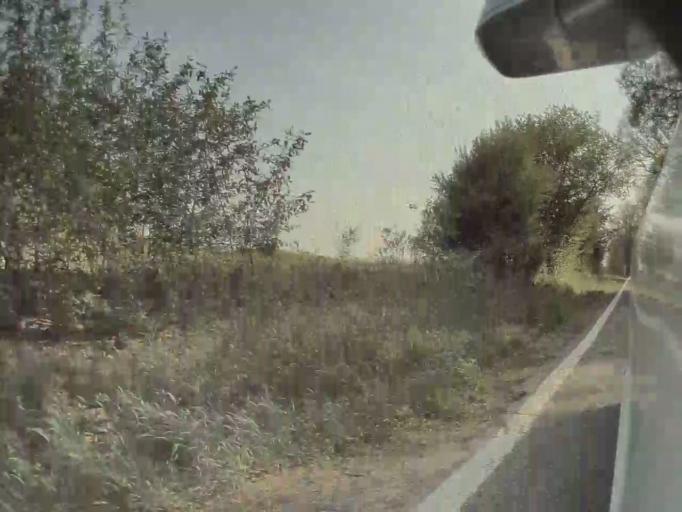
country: BE
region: Wallonia
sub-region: Province de Namur
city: Hamois
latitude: 50.2963
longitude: 5.2086
